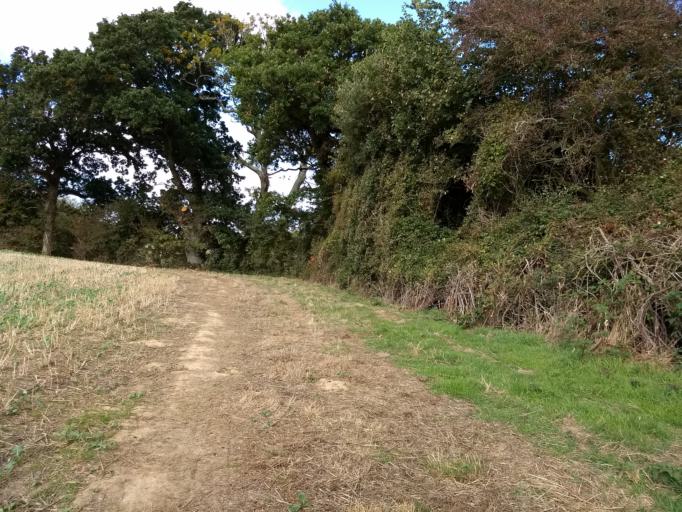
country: GB
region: England
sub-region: Isle of Wight
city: Seaview
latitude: 50.7111
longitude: -1.1234
